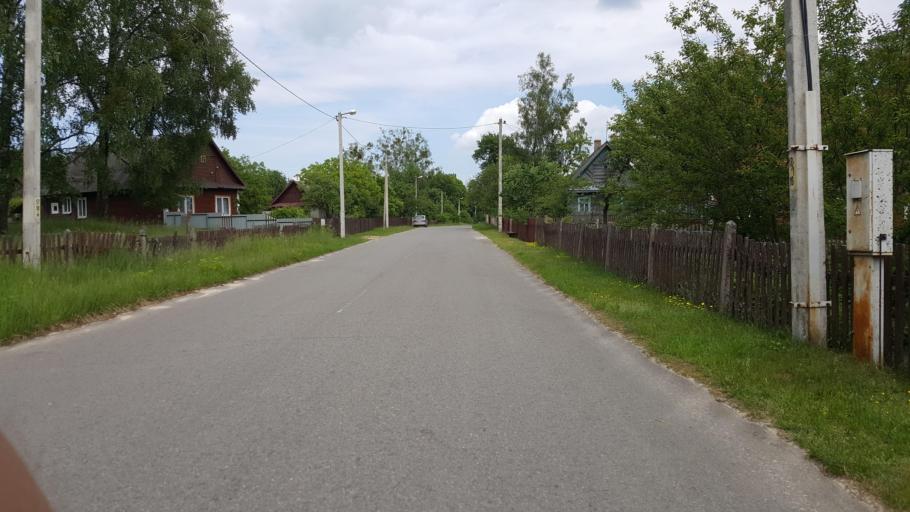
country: PL
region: Podlasie
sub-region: Powiat hajnowski
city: Bialowieza
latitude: 52.6251
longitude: 24.0715
